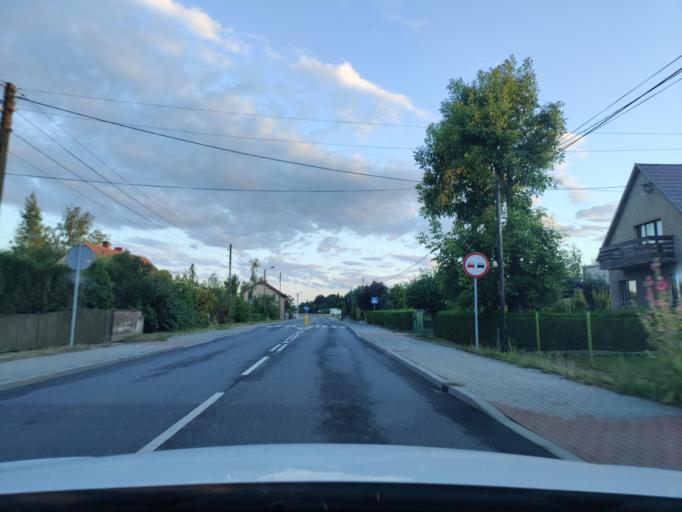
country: PL
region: Opole Voivodeship
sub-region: Powiat nyski
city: Chroscina
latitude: 50.6500
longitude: 17.3844
